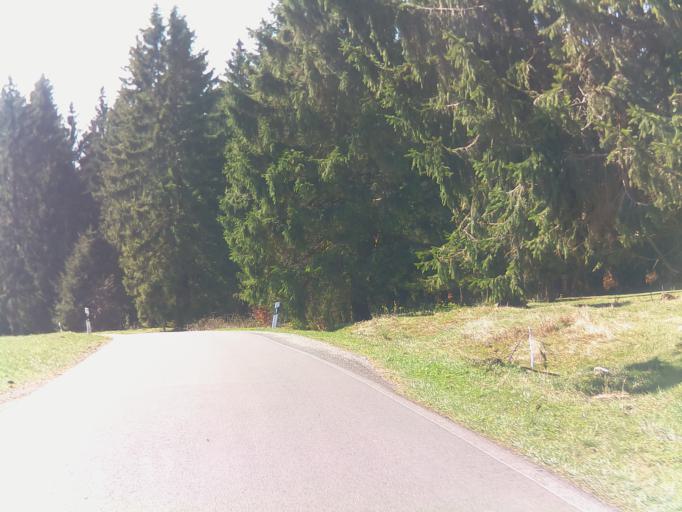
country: DE
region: Thuringia
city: Frauenwald
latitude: 50.5659
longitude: 10.8596
